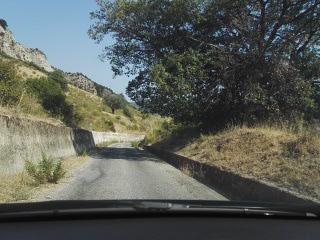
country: IT
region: Calabria
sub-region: Provincia di Reggio Calabria
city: Camini
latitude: 38.4455
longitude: 16.4704
